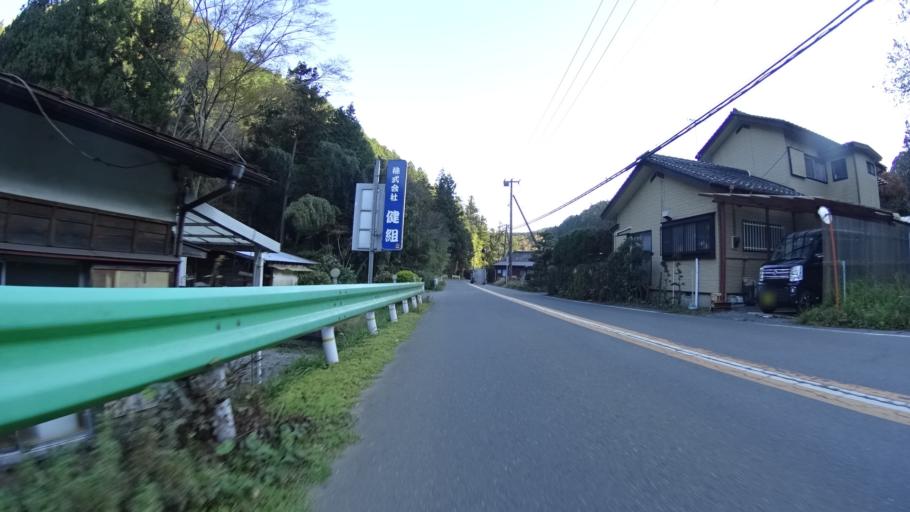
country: JP
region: Tokyo
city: Itsukaichi
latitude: 35.6703
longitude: 139.2333
